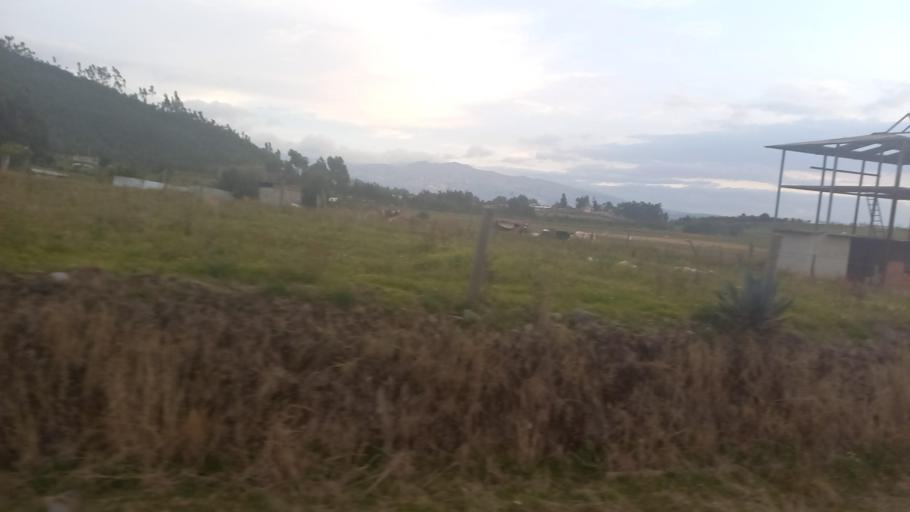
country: EC
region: Pichincha
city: Cayambe
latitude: 0.0708
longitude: -78.1175
